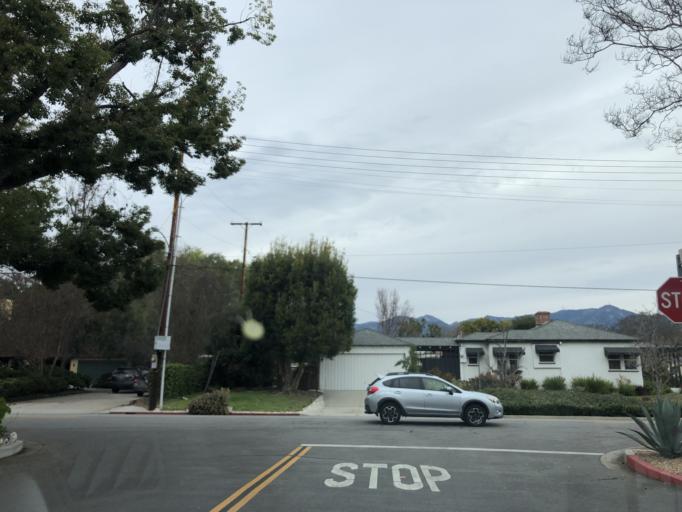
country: US
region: California
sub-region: Los Angeles County
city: San Marino
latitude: 34.1096
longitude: -118.1076
